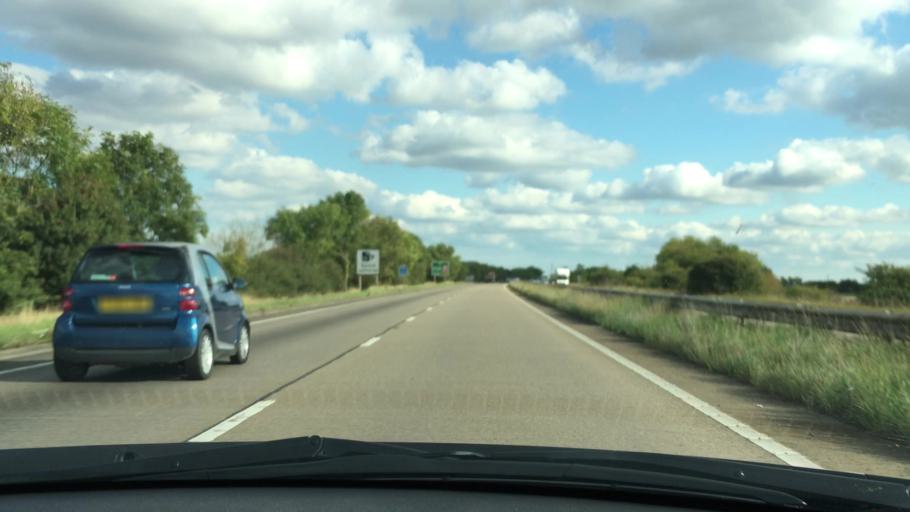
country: GB
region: England
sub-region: North East Lincolnshire
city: Healing
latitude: 53.5924
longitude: -0.1675
